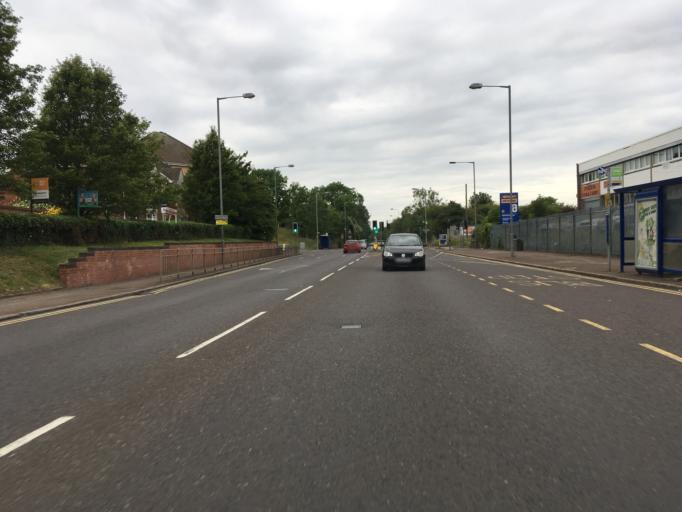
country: GB
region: England
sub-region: Central Bedfordshire
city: Houghton Regis
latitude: 51.8965
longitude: -0.5357
